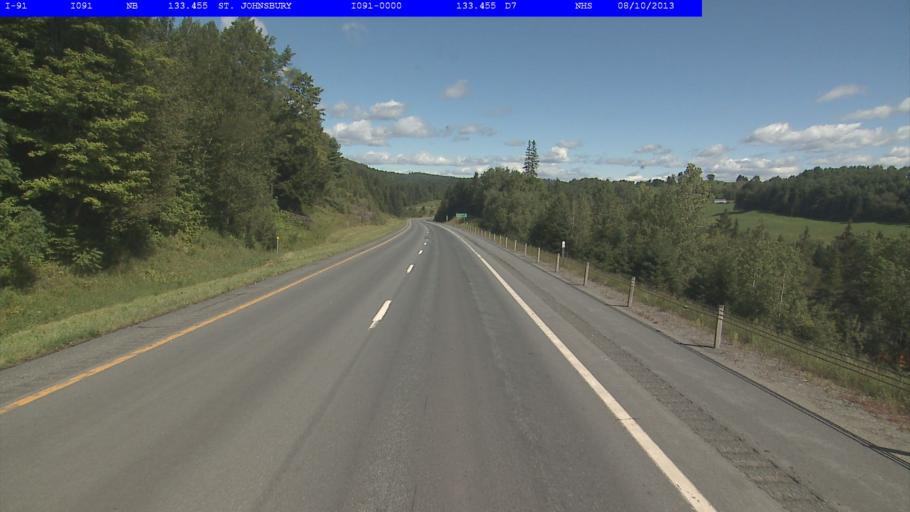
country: US
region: Vermont
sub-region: Caledonia County
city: St Johnsbury
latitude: 44.4667
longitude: -72.0237
